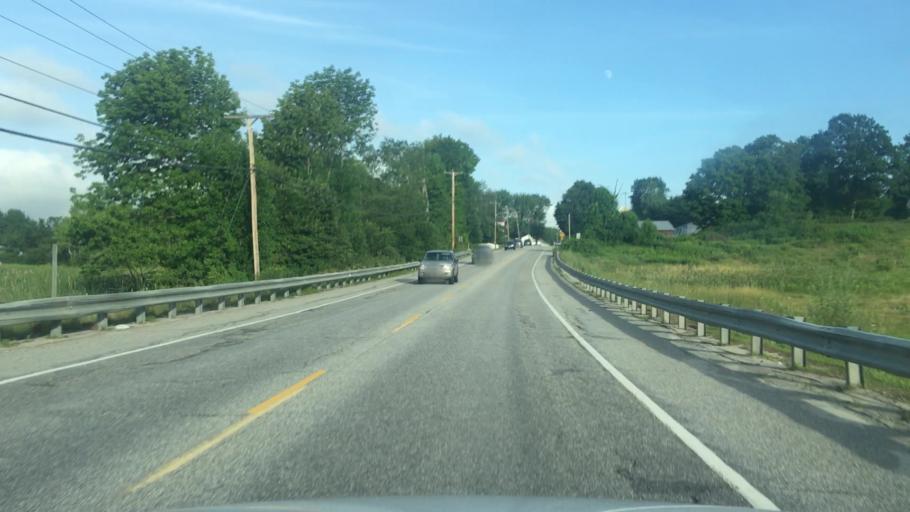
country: US
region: Maine
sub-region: Cumberland County
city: North Windham
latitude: 43.8058
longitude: -70.4098
